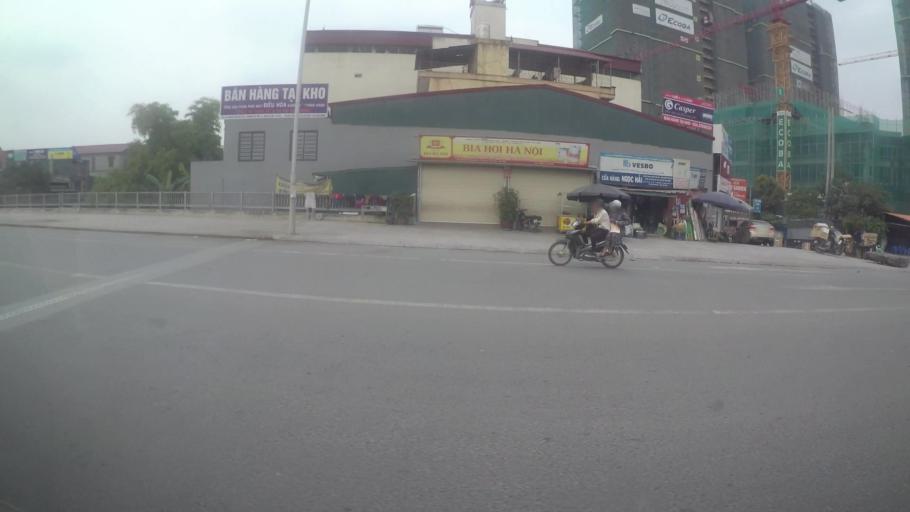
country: VN
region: Ha Noi
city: Cau Dien
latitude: 21.0309
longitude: 105.7589
